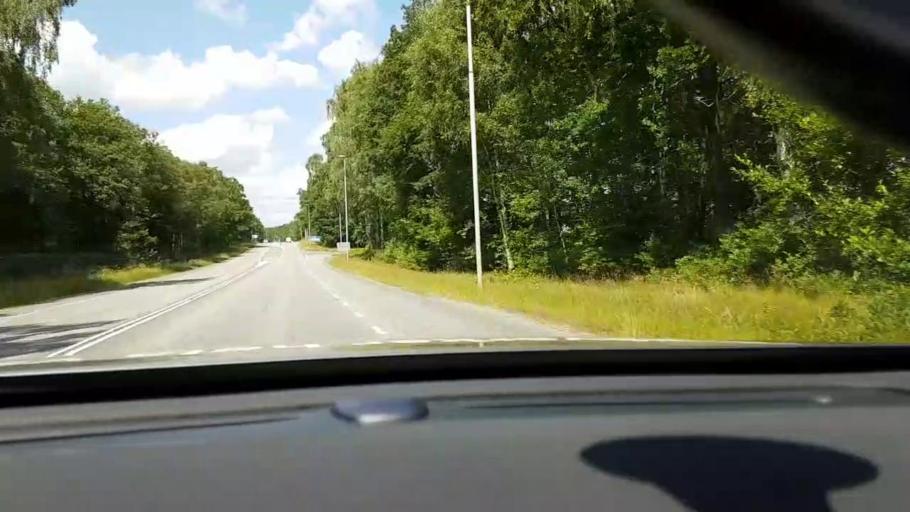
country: SE
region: Skane
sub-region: Hassleholms Kommun
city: Hassleholm
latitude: 56.1622
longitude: 13.7368
